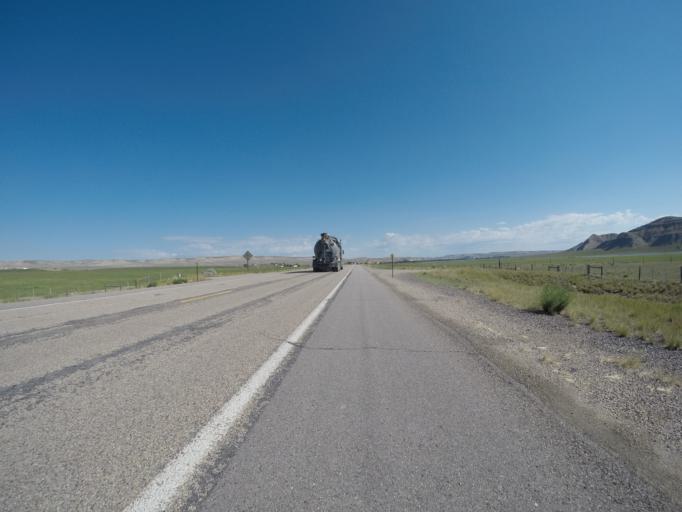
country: US
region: Wyoming
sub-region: Sublette County
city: Marbleton
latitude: 42.1451
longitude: -110.1851
